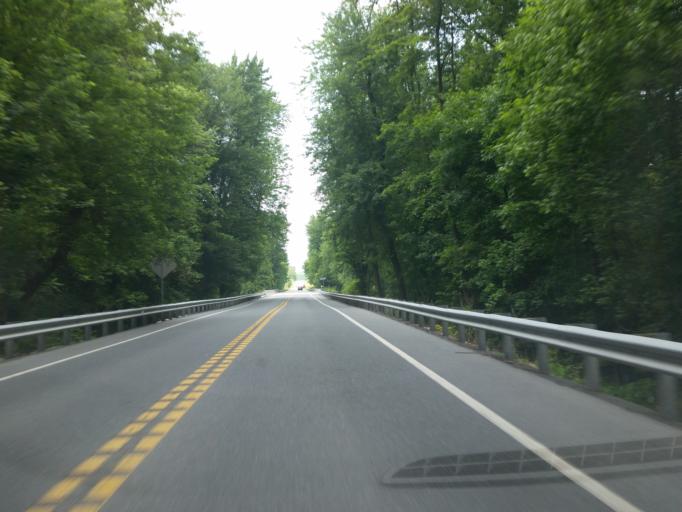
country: US
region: Pennsylvania
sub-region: Lebanon County
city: Palmyra
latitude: 40.3519
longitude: -76.6154
